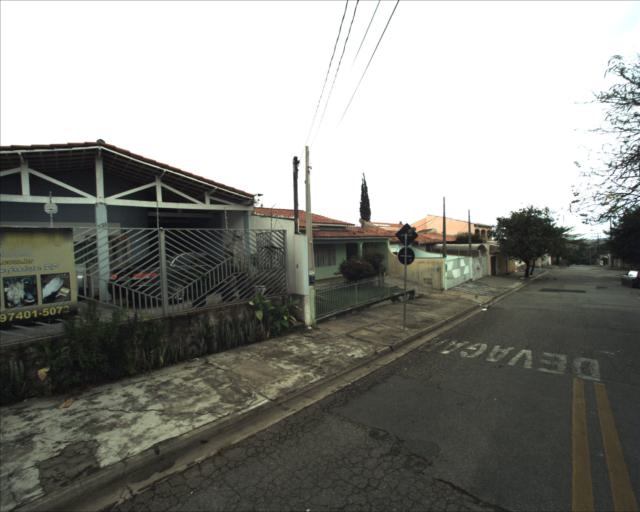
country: BR
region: Sao Paulo
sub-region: Sorocaba
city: Sorocaba
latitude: -23.5026
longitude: -47.4883
